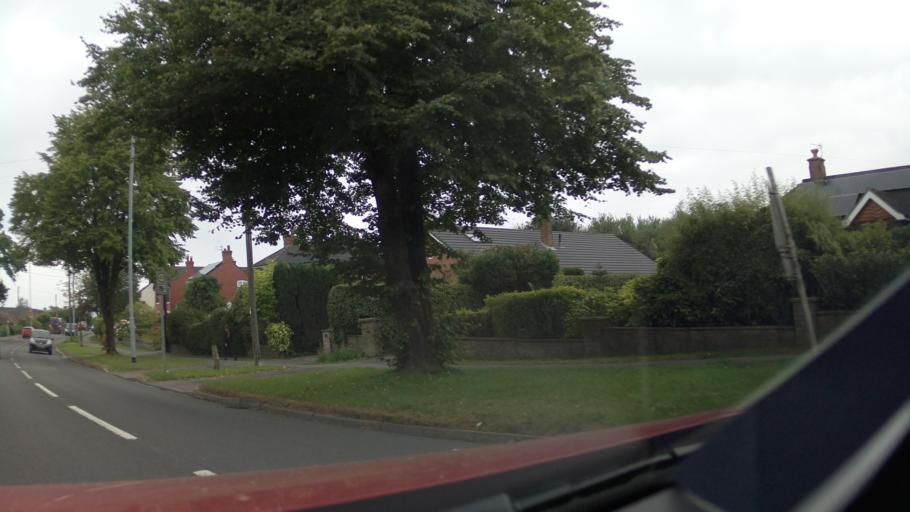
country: GB
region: England
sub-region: Staffordshire
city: Longton
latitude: 53.0222
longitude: -2.0952
